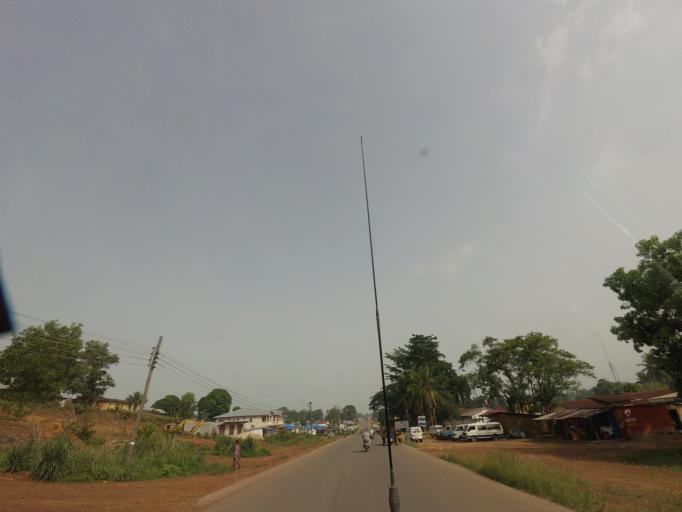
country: SL
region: Southern Province
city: Bo
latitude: 7.9488
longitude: -11.7438
